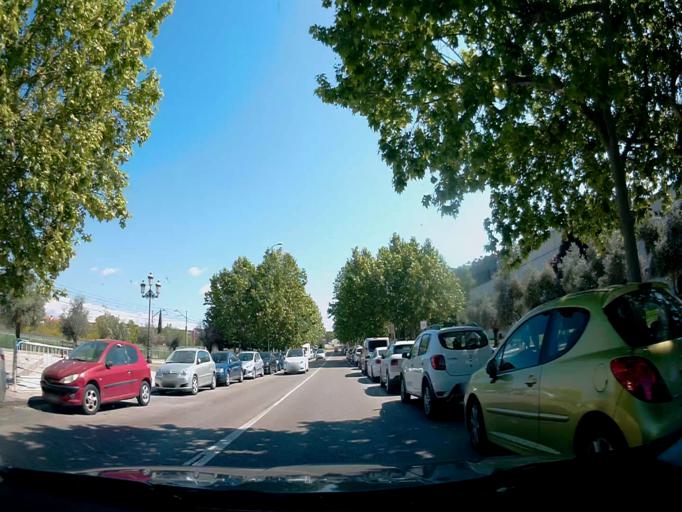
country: ES
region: Madrid
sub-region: Provincia de Madrid
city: Alcorcon
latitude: 40.3478
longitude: -3.8343
